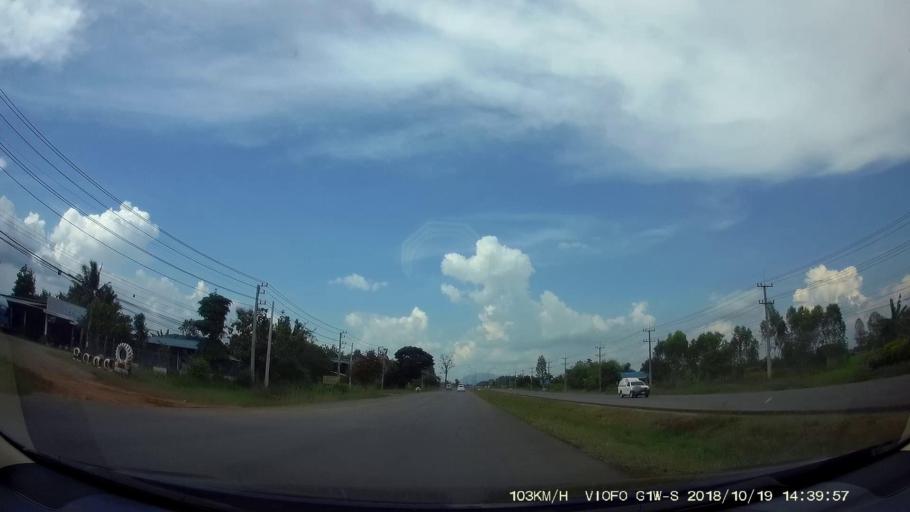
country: TH
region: Chaiyaphum
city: Kaeng Khro
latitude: 16.2336
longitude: 102.1951
